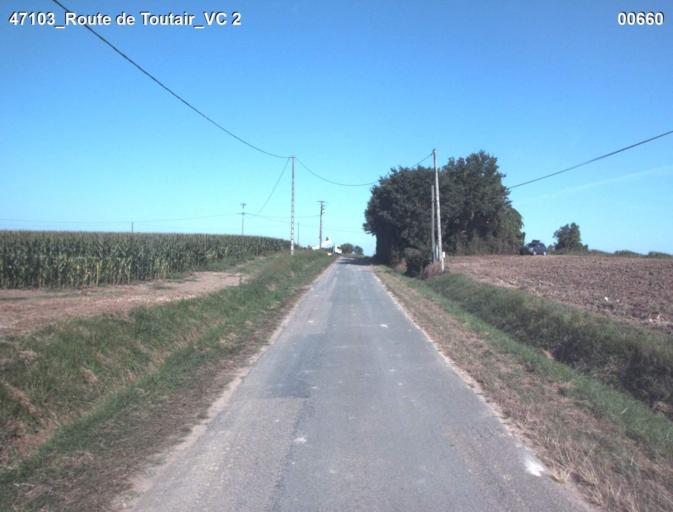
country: FR
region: Aquitaine
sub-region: Departement du Lot-et-Garonne
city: Nerac
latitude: 44.0794
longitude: 0.3228
